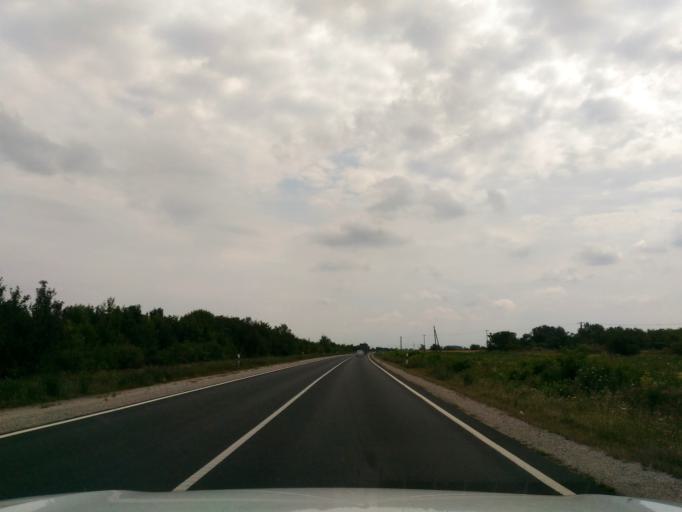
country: HU
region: Pest
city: Abony
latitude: 47.2124
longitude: 19.9703
